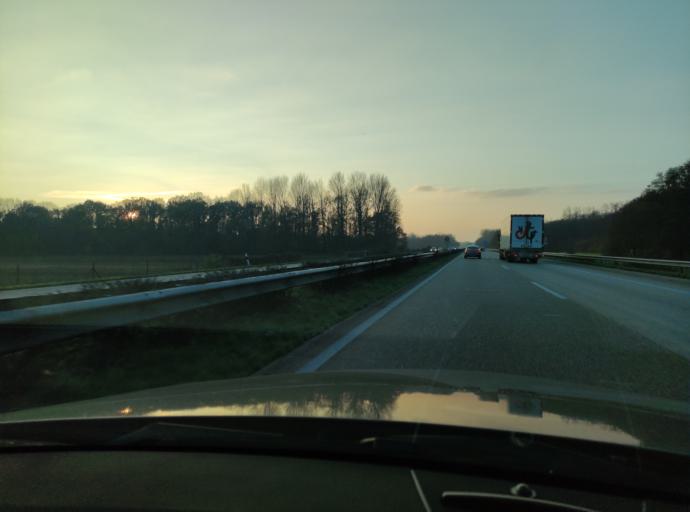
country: DE
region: North Rhine-Westphalia
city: Kempen
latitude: 51.4100
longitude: 6.4385
